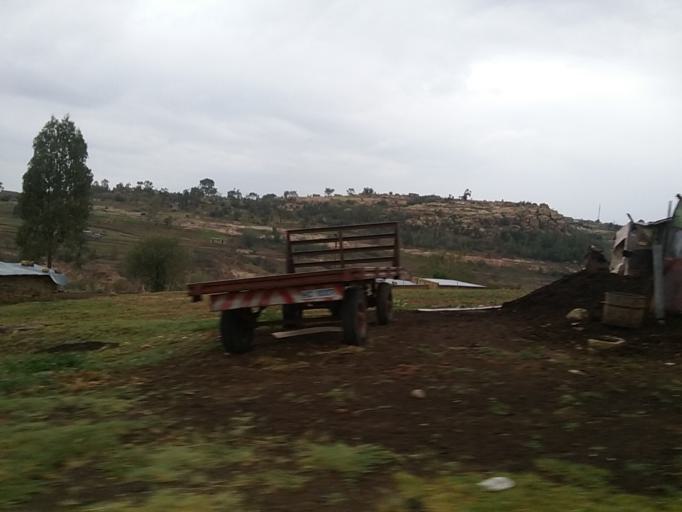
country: LS
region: Berea
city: Teyateyaneng
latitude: -29.1338
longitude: 27.7387
